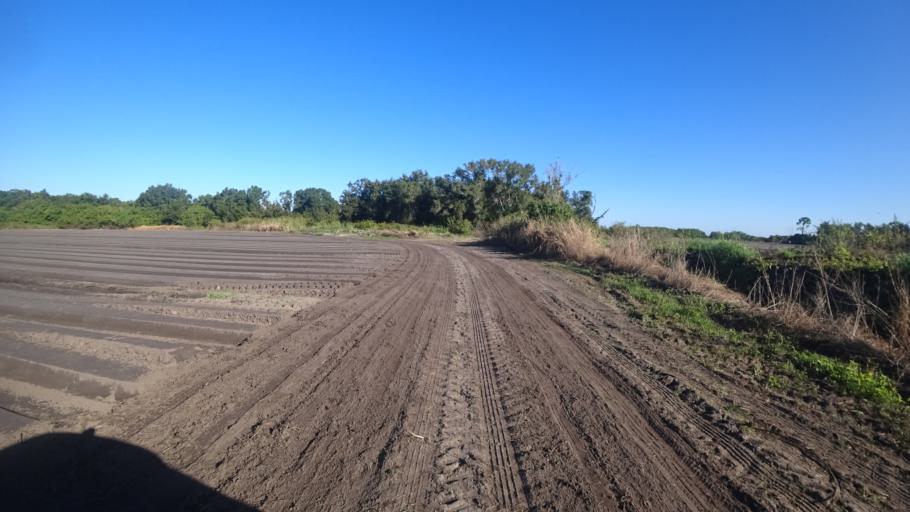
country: US
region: Florida
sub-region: Hillsborough County
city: Ruskin
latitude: 27.6439
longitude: -82.4359
